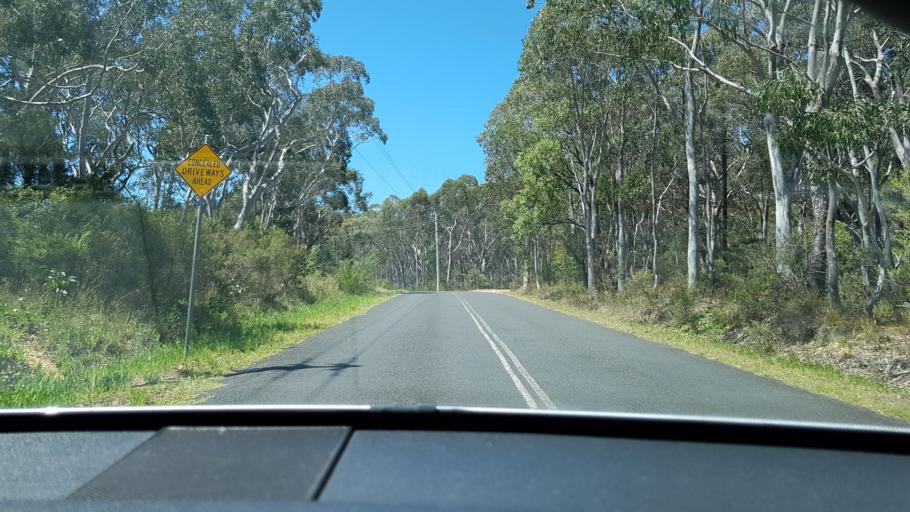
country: AU
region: New South Wales
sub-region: Blue Mountains Municipality
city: Katoomba
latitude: -33.7005
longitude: 150.2509
